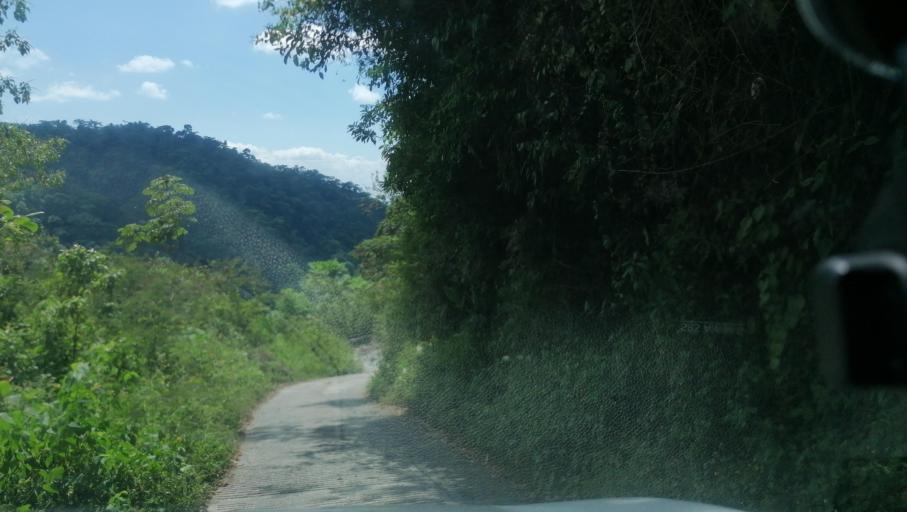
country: MX
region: Chiapas
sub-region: Union Juarez
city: Santo Domingo
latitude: 15.0783
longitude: -92.1283
